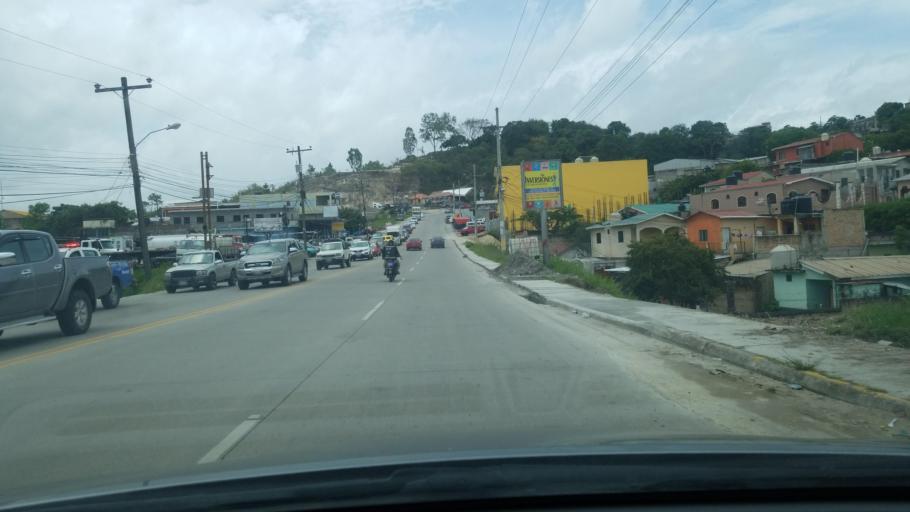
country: HN
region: Copan
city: Santa Rosa de Copan
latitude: 14.7706
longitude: -88.7731
